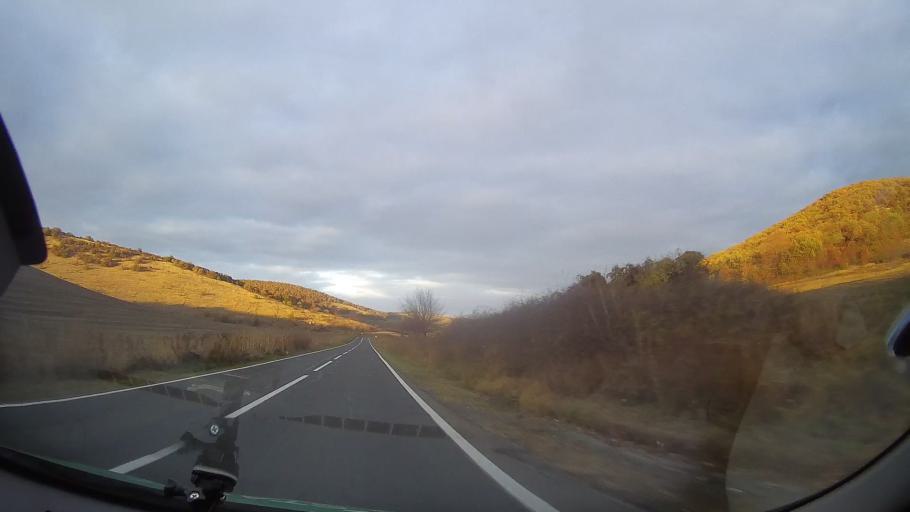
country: RO
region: Tulcea
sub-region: Comuna Ciucurova
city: Ciucurova
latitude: 44.9587
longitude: 28.5181
